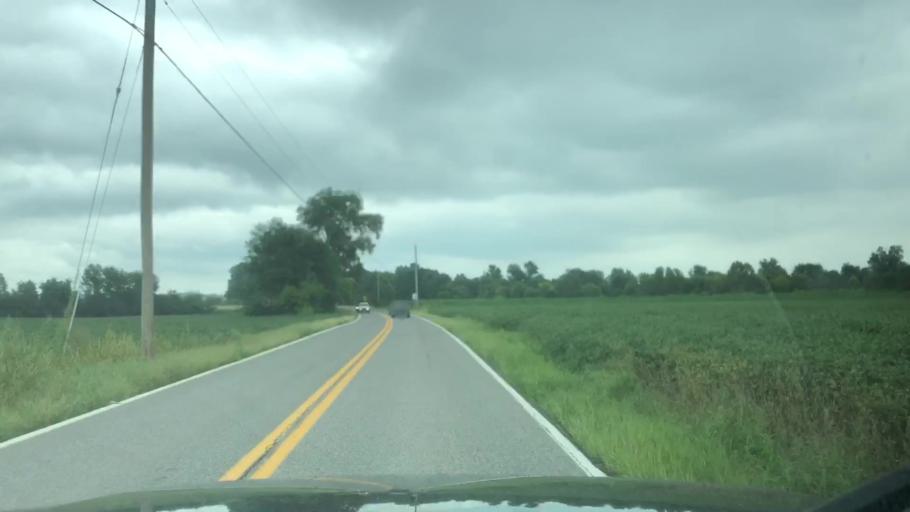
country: US
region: Missouri
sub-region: Saint Louis County
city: Bridgeton
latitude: 38.7972
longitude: -90.4238
